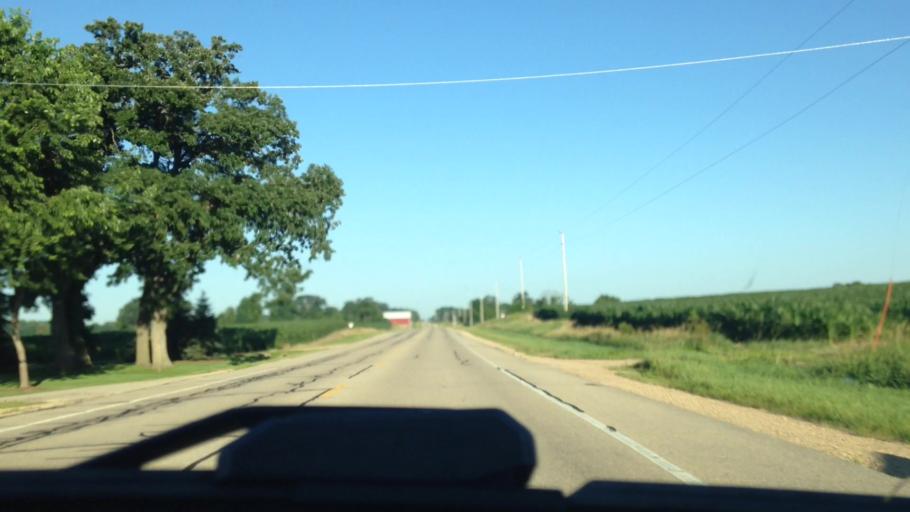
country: US
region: Wisconsin
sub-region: Columbia County
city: Columbus
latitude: 43.3417
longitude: -89.0536
